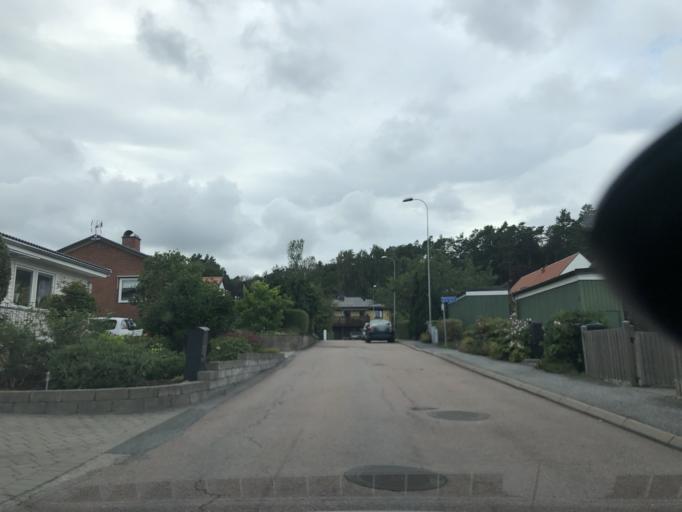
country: SE
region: Vaestra Goetaland
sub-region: Goteborg
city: Goeteborg
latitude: 57.7555
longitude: 11.9600
